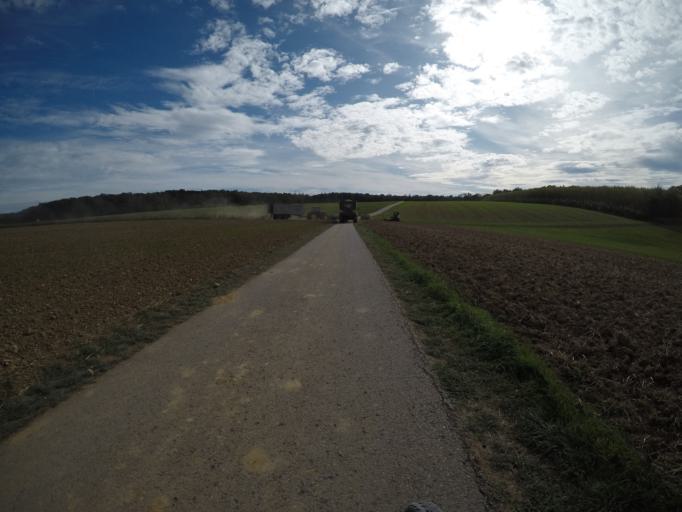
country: DE
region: Baden-Wuerttemberg
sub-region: Regierungsbezirk Stuttgart
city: Eberdingen
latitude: 48.8413
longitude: 8.9731
